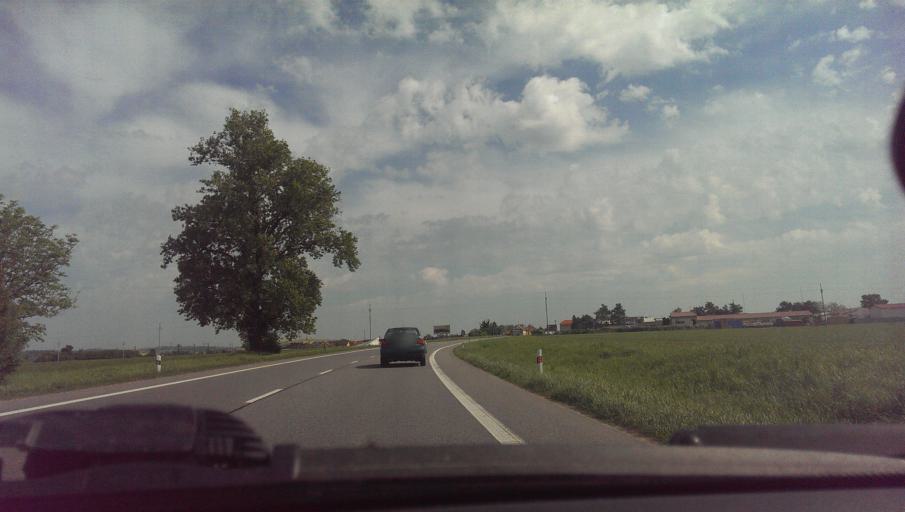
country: CZ
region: Zlin
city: Babice
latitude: 49.1030
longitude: 17.4571
